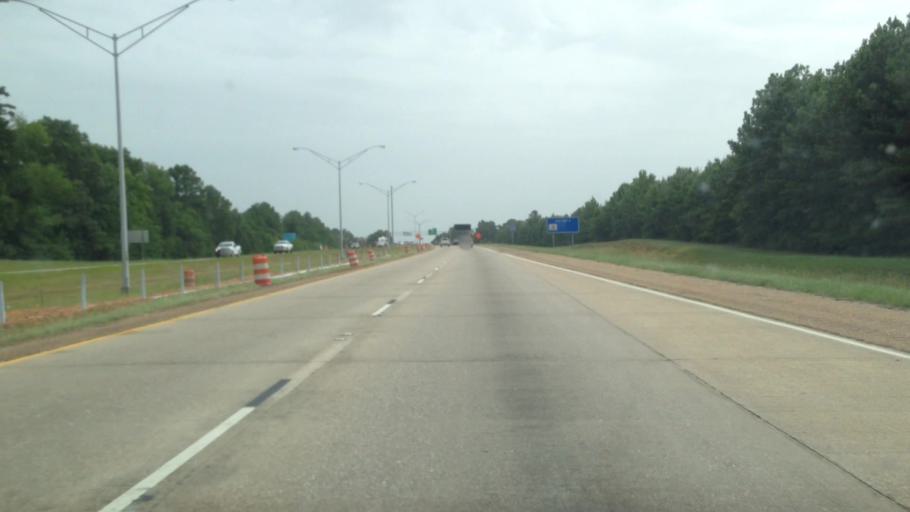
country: US
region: Louisiana
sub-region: Caddo Parish
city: Shreveport
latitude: 32.4902
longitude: -93.8247
